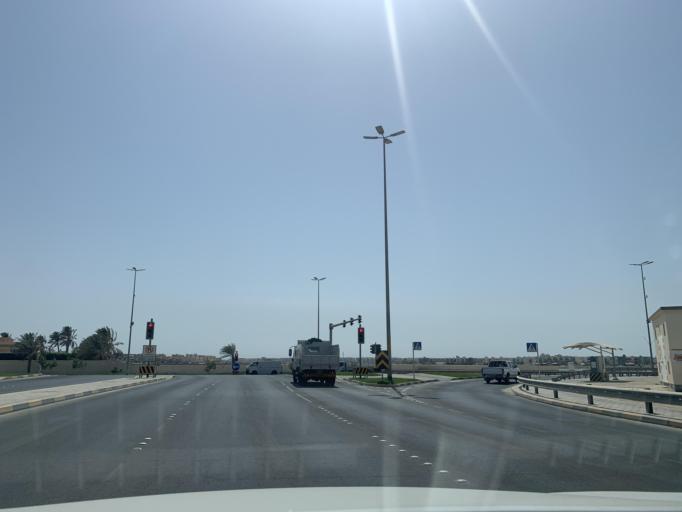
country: BH
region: Manama
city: Jidd Hafs
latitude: 26.2206
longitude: 50.4554
